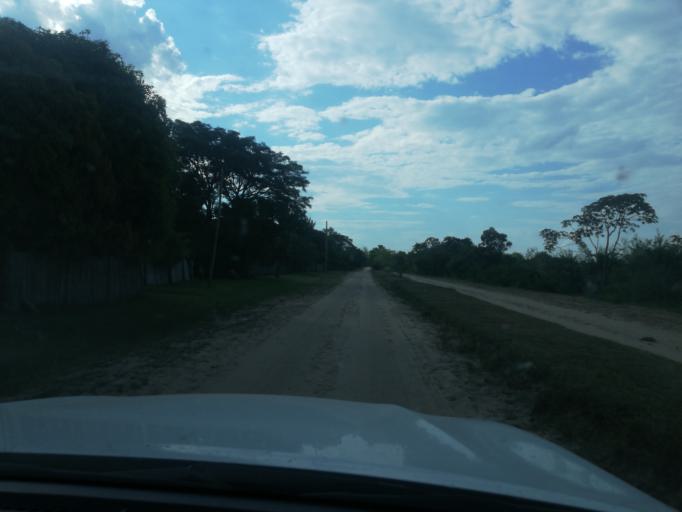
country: AR
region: Corrientes
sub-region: Departamento de San Miguel
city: San Miguel
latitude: -27.9966
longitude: -57.5822
